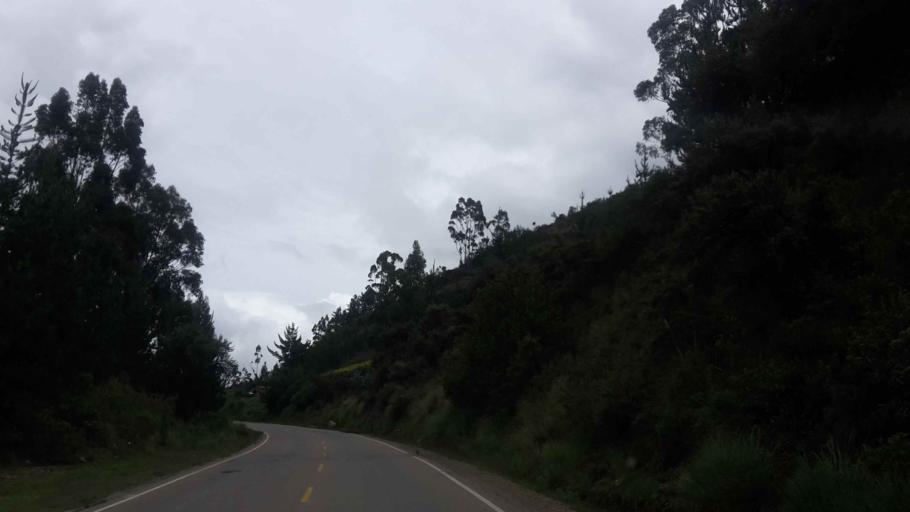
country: BO
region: Cochabamba
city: Arani
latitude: -17.4860
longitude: -65.4695
